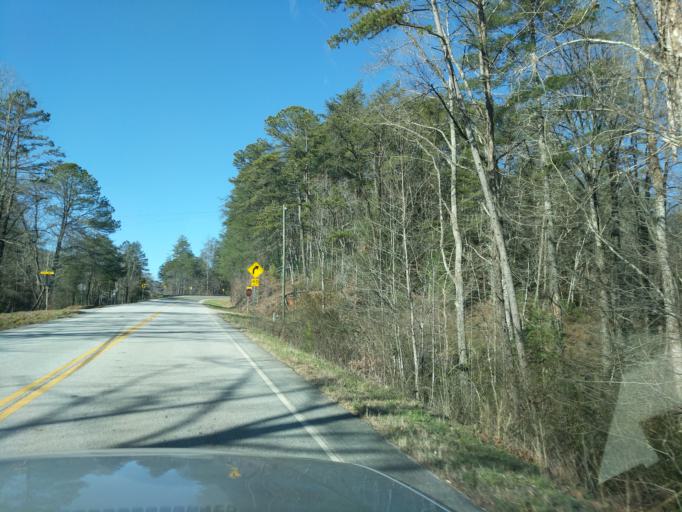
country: US
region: Georgia
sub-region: Rabun County
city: Clayton
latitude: 34.8478
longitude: -83.3589
